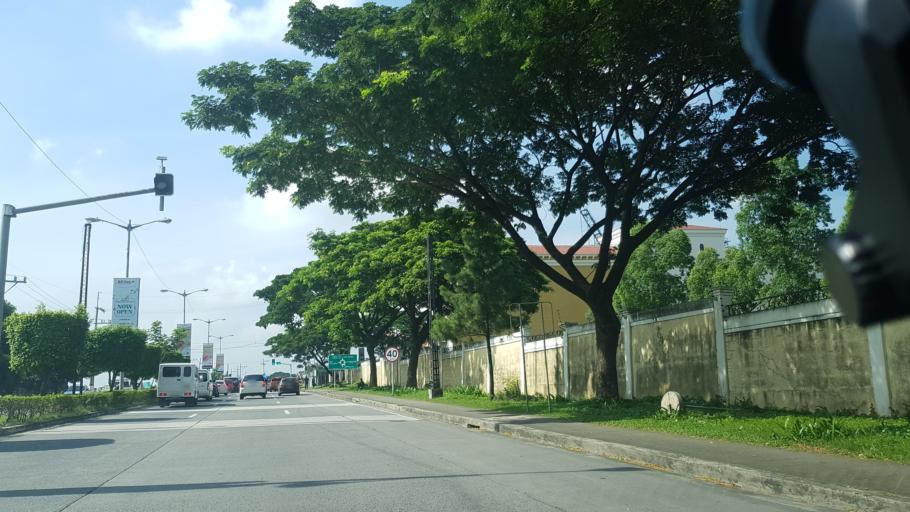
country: PH
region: Calabarzon
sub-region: Province of Laguna
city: San Pedro
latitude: 14.3779
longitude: 121.0130
